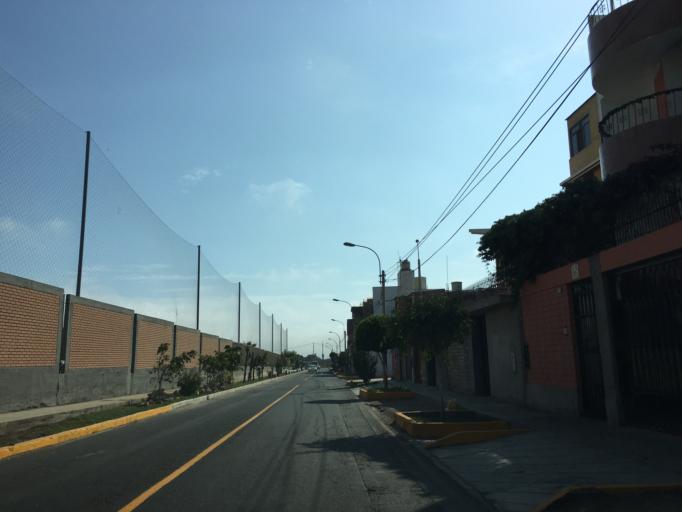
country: PE
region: Callao
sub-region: Callao
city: Callao
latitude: -12.0645
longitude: -77.0794
